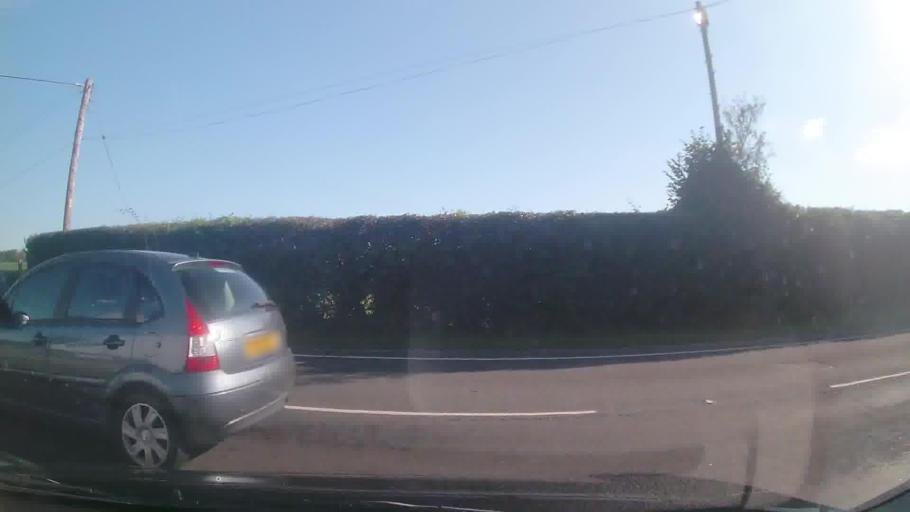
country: GB
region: England
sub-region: Cumbria
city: Seascale
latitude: 54.3814
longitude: -3.4144
